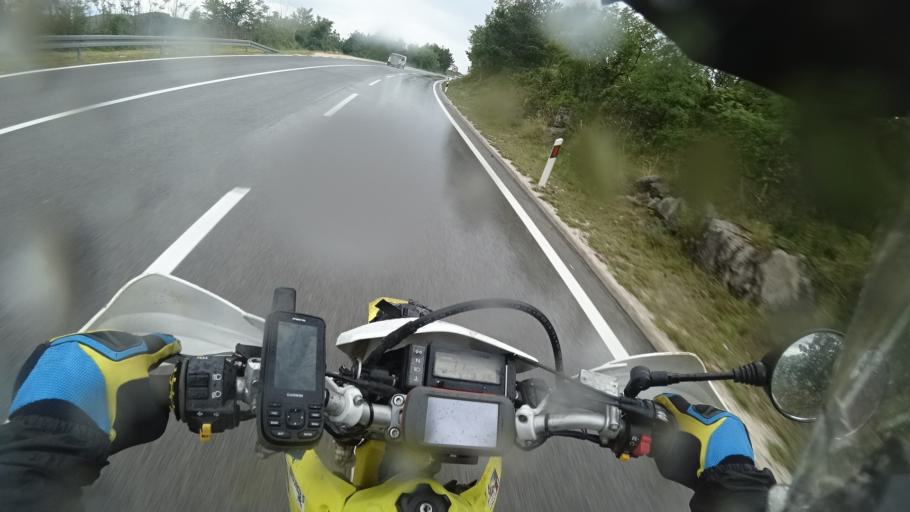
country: HR
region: Sibensko-Kniniska
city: Knin
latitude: 44.0423
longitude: 16.1855
